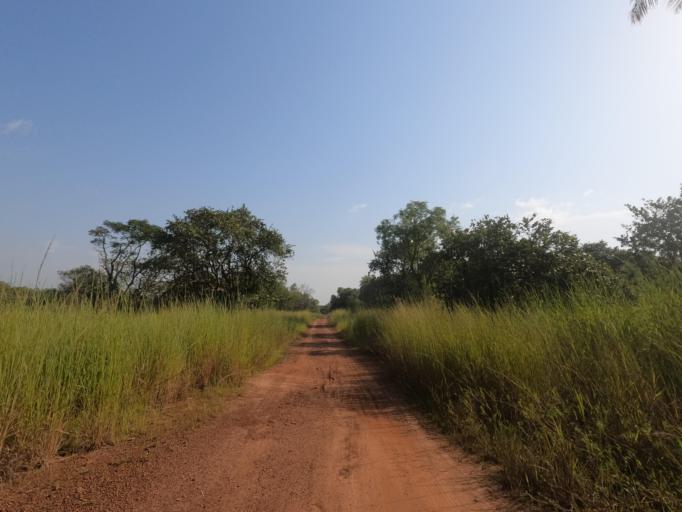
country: SN
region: Sedhiou
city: Sedhiou
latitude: 12.4359
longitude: -15.7380
